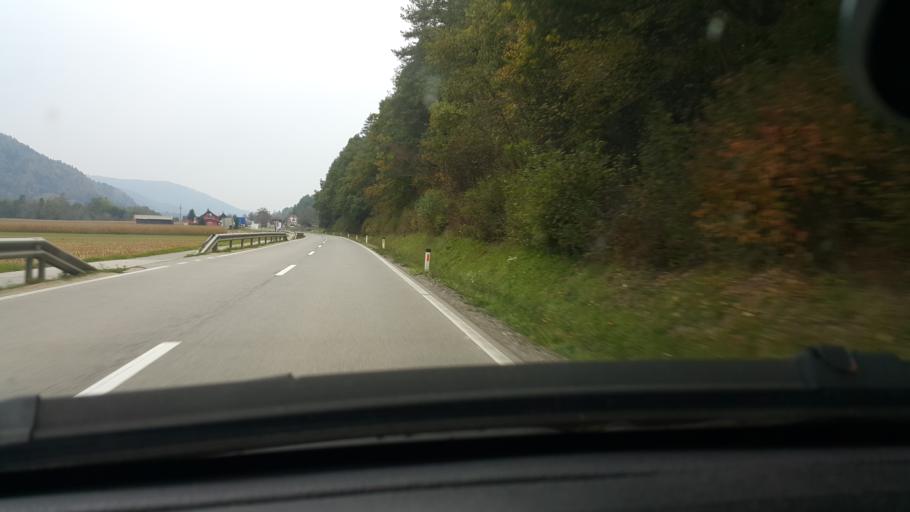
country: SI
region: Dravograd
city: Dravograd
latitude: 46.6009
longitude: 14.9911
